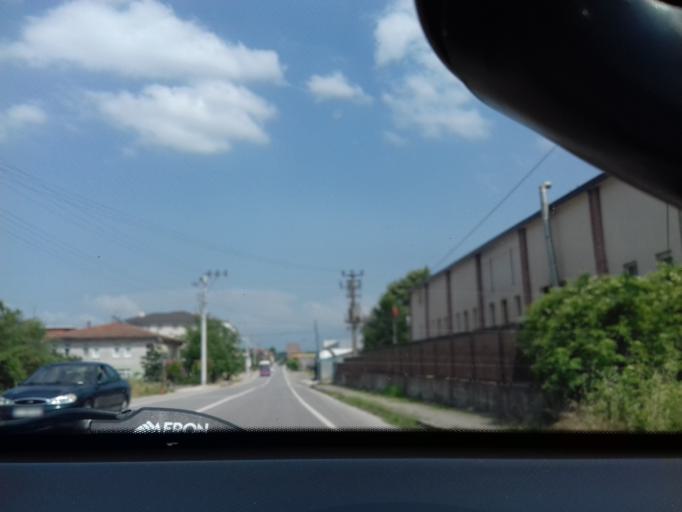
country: TR
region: Sakarya
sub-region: Merkez
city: Sapanca
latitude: 40.7136
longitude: 30.3475
